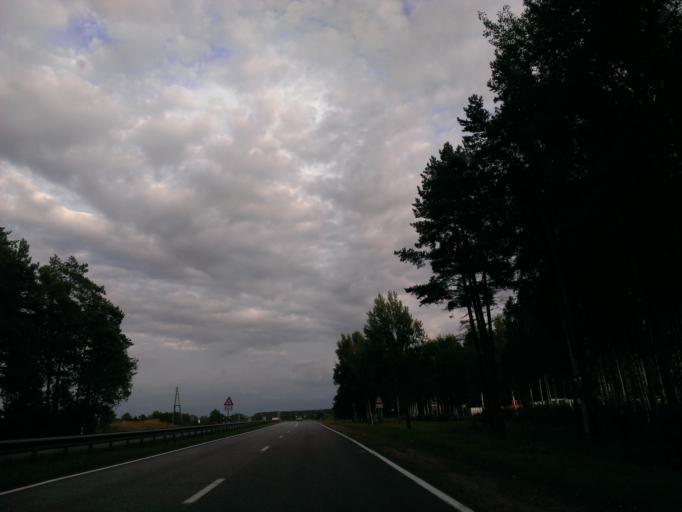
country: LV
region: Ikskile
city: Ikskile
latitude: 56.8244
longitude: 24.5304
